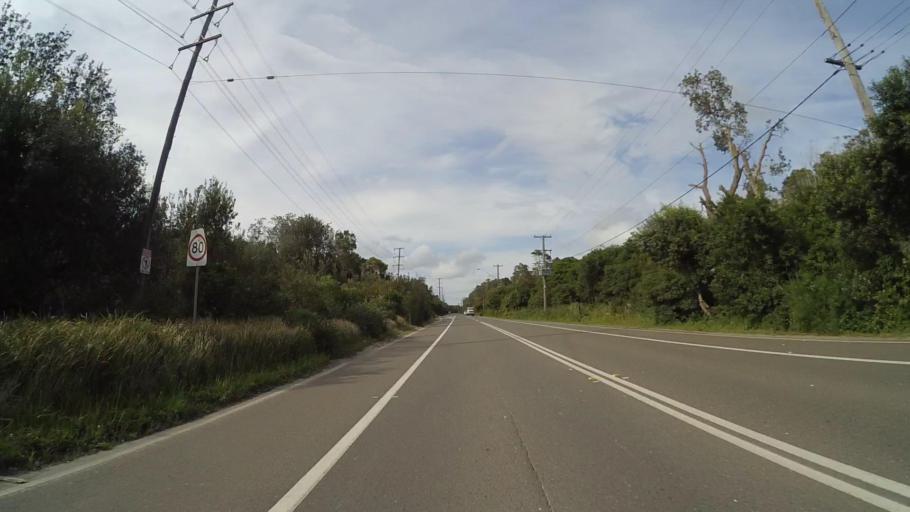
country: AU
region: New South Wales
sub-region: Rockdale
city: Dolls Point
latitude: -34.0259
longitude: 151.1637
